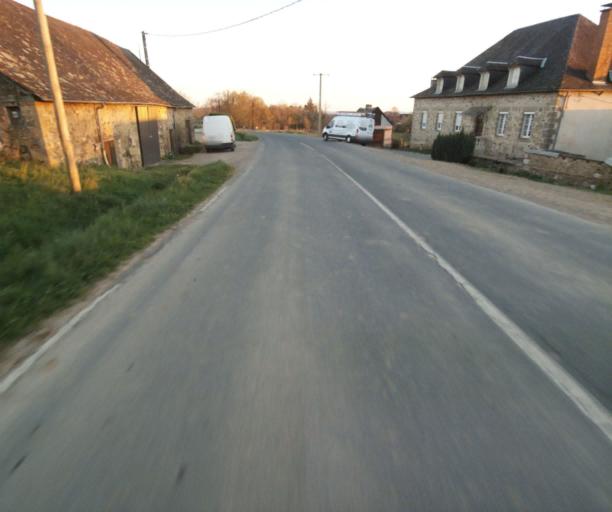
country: FR
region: Limousin
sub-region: Departement de la Correze
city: Sainte-Fereole
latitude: 45.2751
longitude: 1.5627
